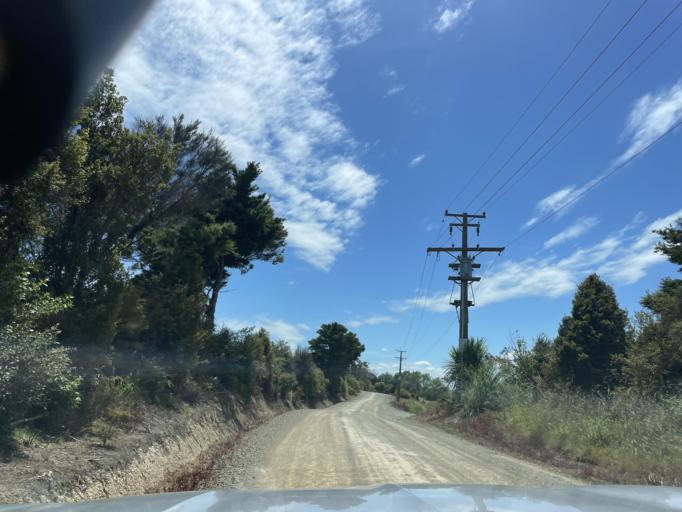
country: NZ
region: Auckland
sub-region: Auckland
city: Wellsford
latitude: -36.2212
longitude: 174.3612
